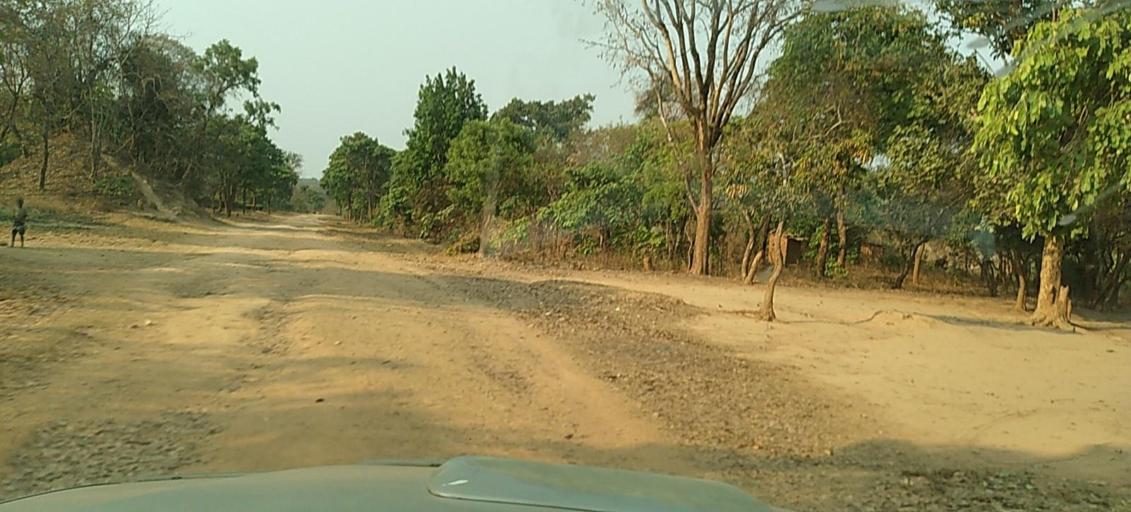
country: ZM
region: North-Western
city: Kasempa
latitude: -13.2738
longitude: 26.5565
